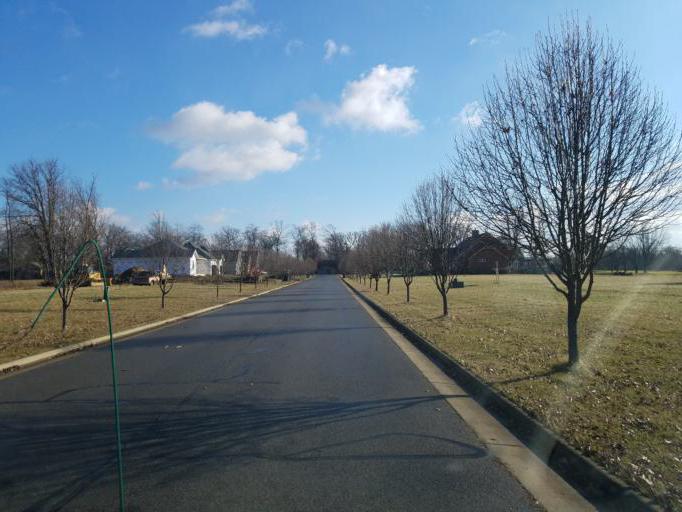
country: US
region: Ohio
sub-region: Marion County
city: Marion
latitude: 40.5424
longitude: -83.1580
